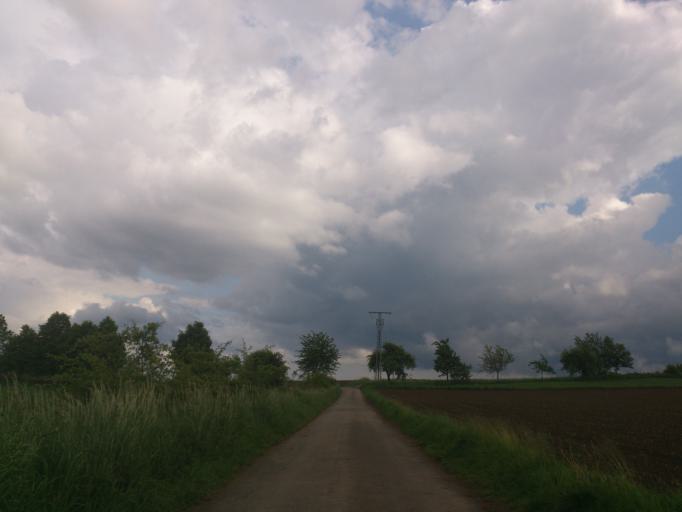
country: DE
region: North Rhine-Westphalia
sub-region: Regierungsbezirk Detmold
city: Willebadessen
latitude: 51.5760
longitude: 9.0357
